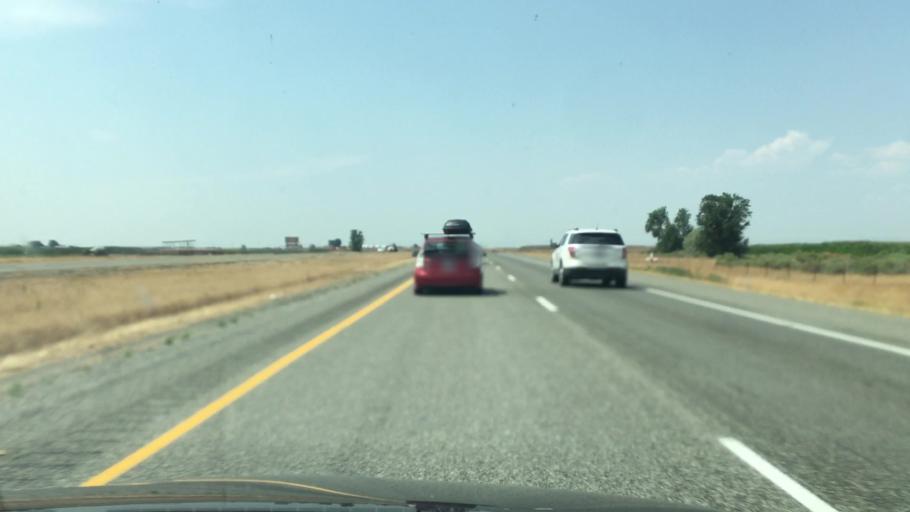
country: US
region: Idaho
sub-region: Gooding County
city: Wendell
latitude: 42.7981
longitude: -114.7560
